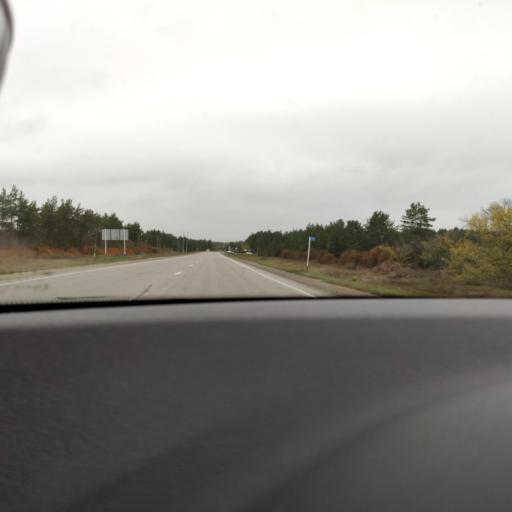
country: RU
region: Samara
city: Mirnyy
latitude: 53.5268
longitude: 50.3123
